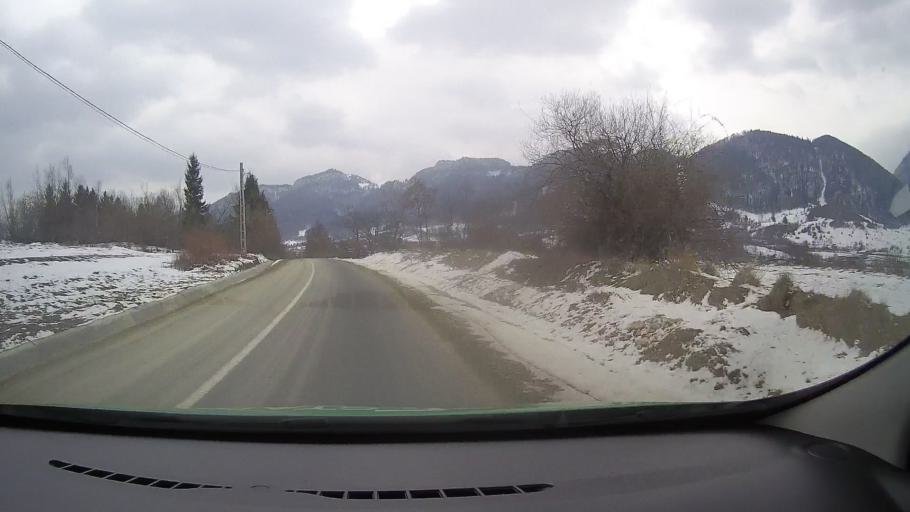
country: RO
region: Brasov
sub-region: Comuna Zarnesti
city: Zarnesti
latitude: 45.5486
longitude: 25.3219
